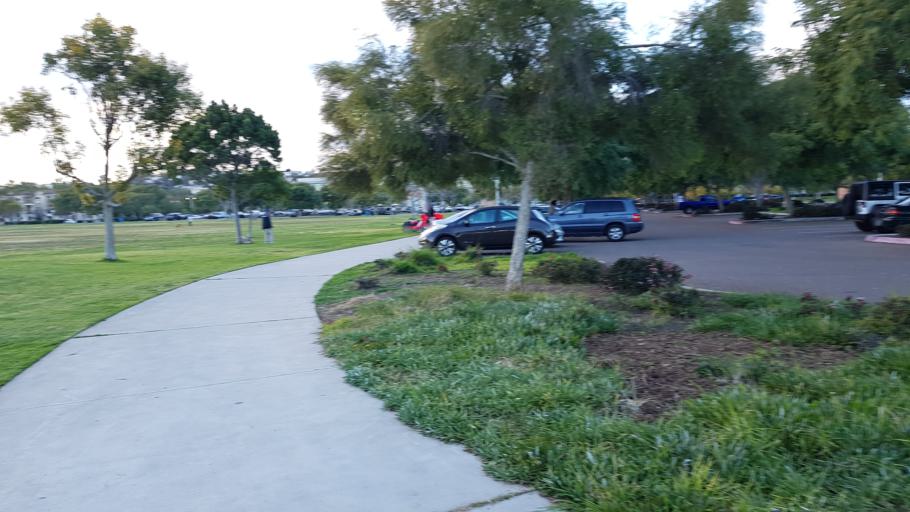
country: US
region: California
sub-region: San Diego County
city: Coronado
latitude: 32.7328
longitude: -117.2140
